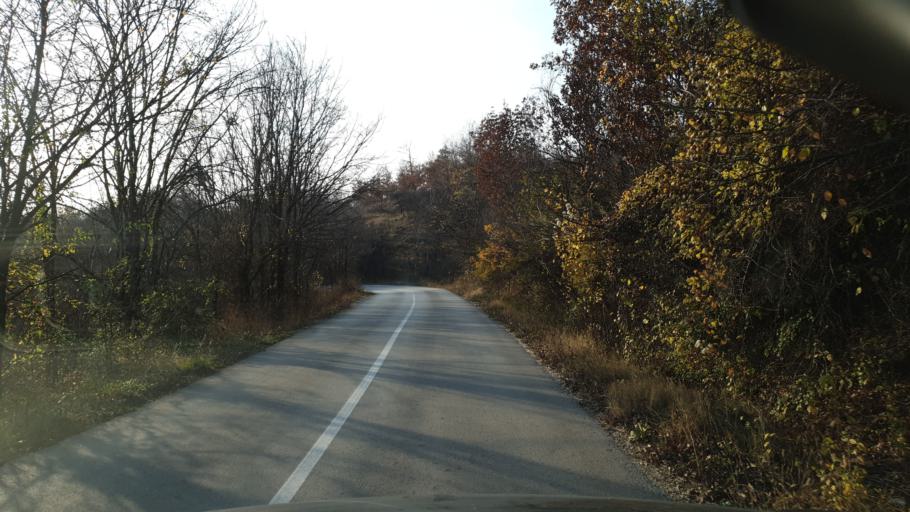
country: RS
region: Central Serbia
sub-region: Borski Okrug
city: Bor
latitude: 44.0472
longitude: 22.0825
